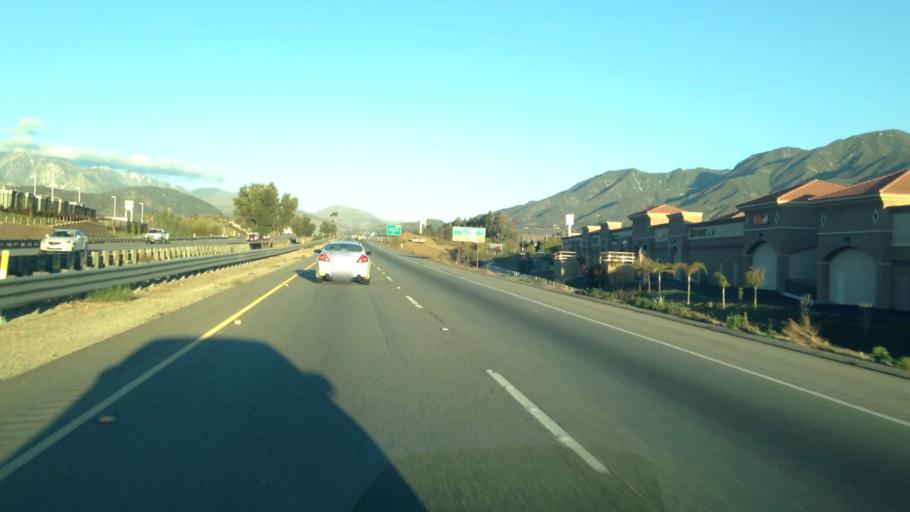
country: US
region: California
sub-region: San Bernardino County
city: Muscoy
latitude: 34.1874
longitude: -117.3561
